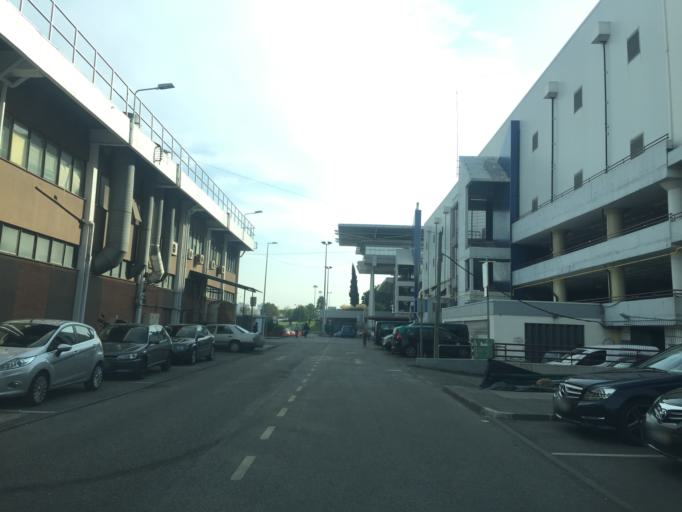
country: PT
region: Lisbon
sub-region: Loures
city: Moscavide
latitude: 38.7723
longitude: -9.1283
